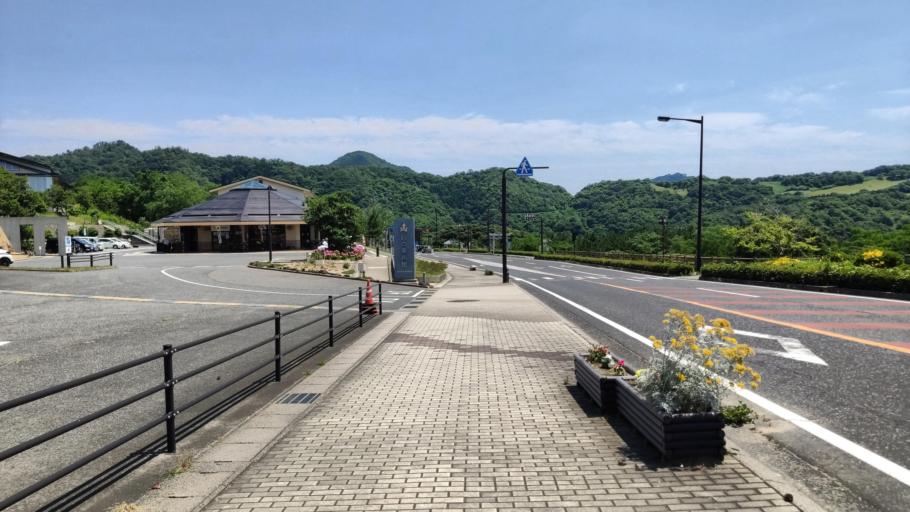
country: JP
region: Tottori
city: Tottori
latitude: 35.5403
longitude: 134.2368
